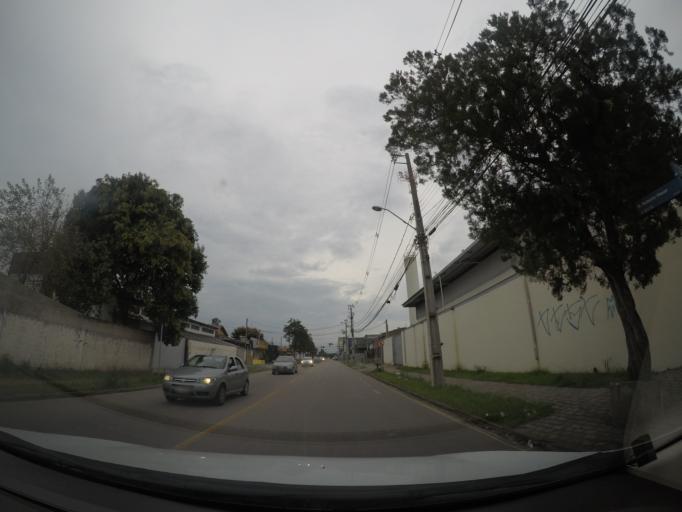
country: BR
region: Parana
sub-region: Curitiba
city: Curitiba
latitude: -25.4720
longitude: -49.2494
